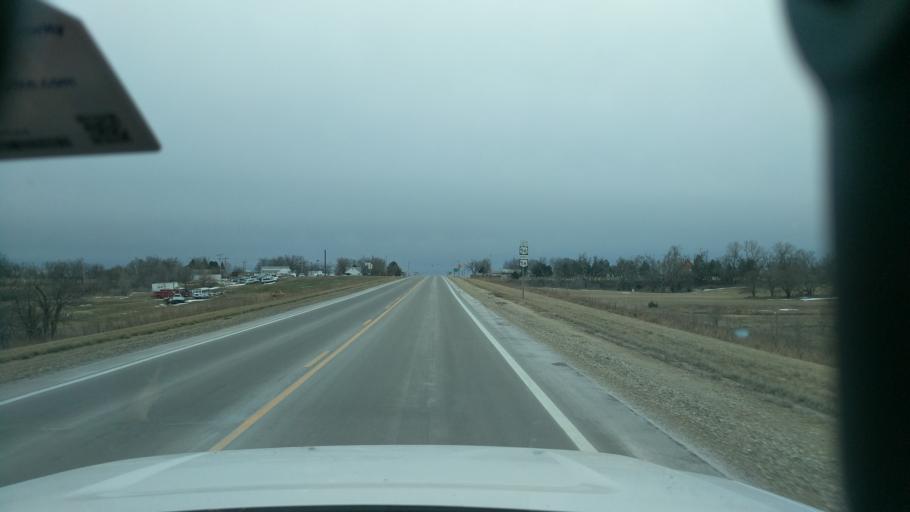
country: US
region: Kansas
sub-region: Dickinson County
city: Herington
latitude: 38.6709
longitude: -96.9313
